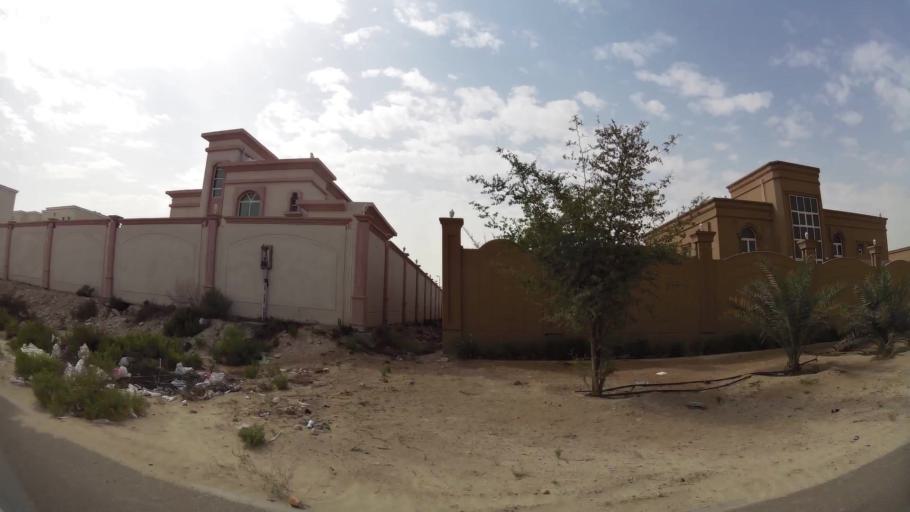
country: AE
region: Abu Dhabi
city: Abu Dhabi
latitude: 24.2765
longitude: 54.6635
